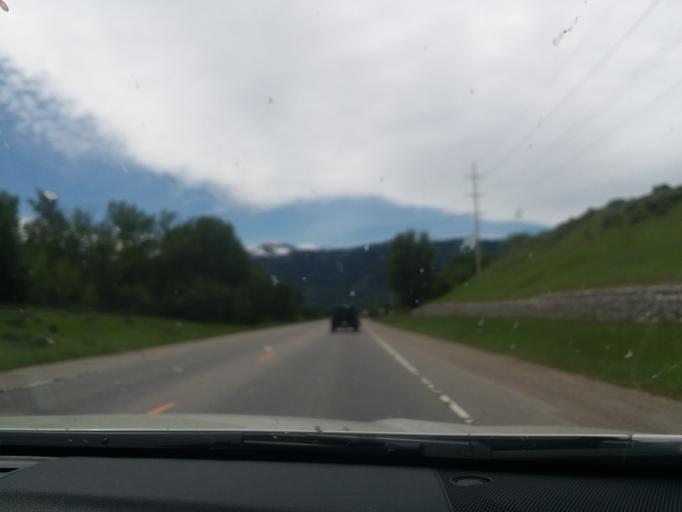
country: US
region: Wyoming
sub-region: Teton County
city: Moose Wilson Road
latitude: 43.4979
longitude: -110.8342
